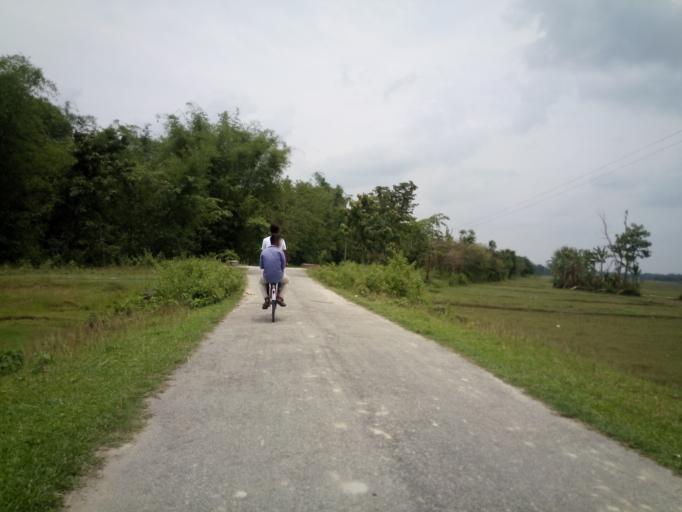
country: IN
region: Assam
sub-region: Udalguri
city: Udalguri
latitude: 26.6943
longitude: 92.0776
